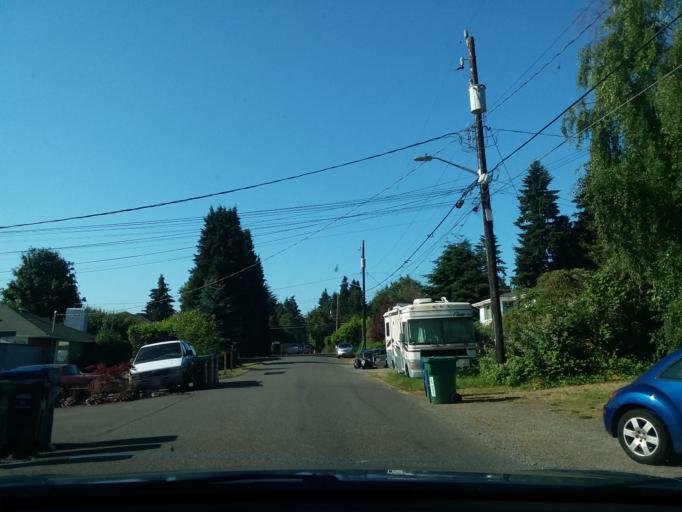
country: US
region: Washington
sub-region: King County
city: Shoreline
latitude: 47.7259
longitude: -122.3263
